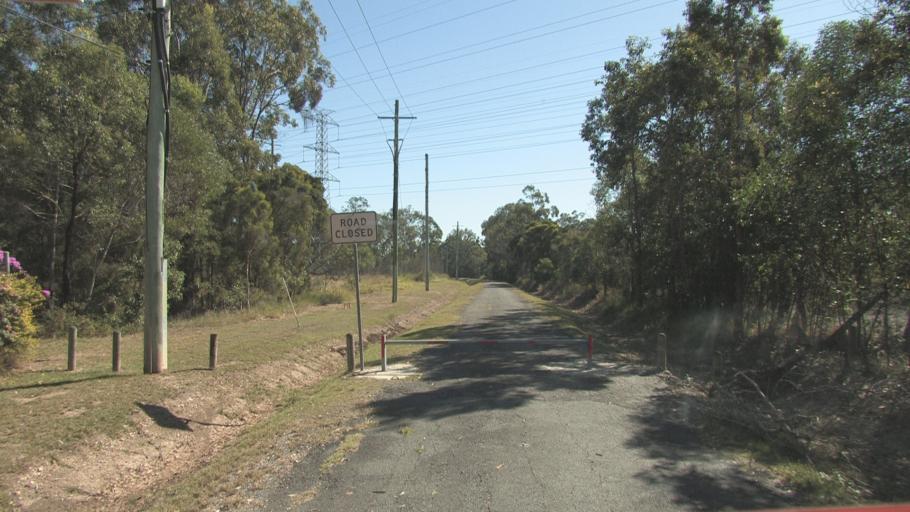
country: AU
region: Queensland
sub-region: Logan
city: Slacks Creek
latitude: -27.6637
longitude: 153.1282
